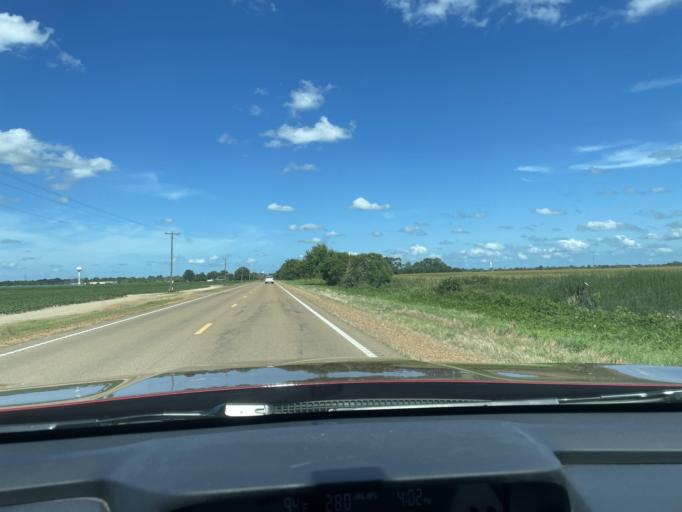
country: US
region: Mississippi
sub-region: Humphreys County
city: Belzoni
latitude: 33.1838
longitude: -90.5125
